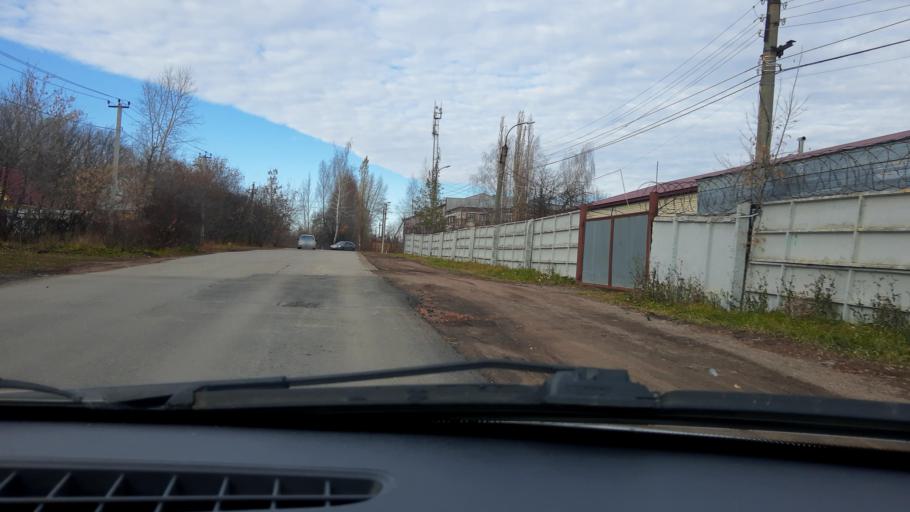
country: RU
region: Bashkortostan
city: Avdon
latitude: 54.6849
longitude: 55.7946
